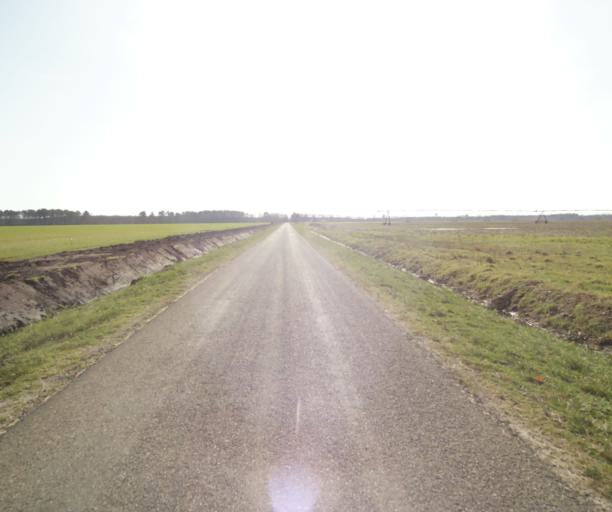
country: FR
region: Aquitaine
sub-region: Departement des Landes
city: Roquefort
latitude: 44.1538
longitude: -0.1707
